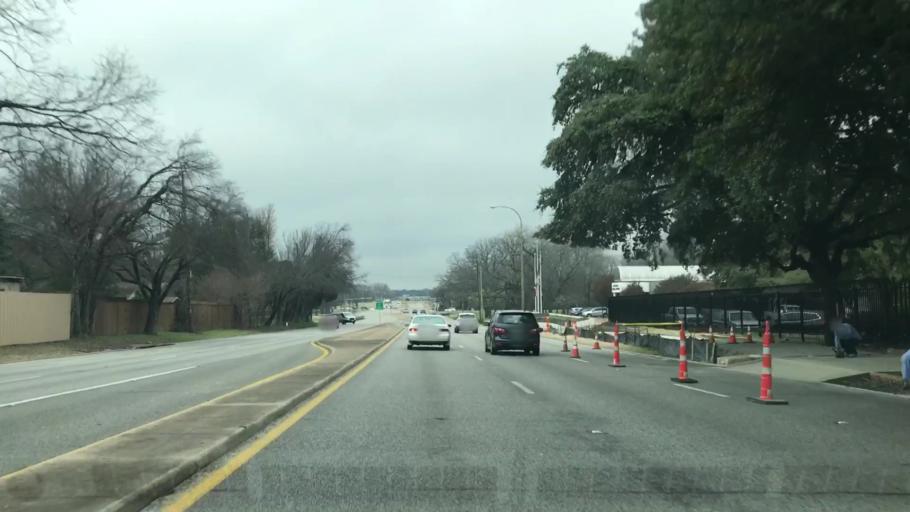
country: US
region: Texas
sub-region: Dallas County
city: Highland Park
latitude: 32.8635
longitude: -96.7145
